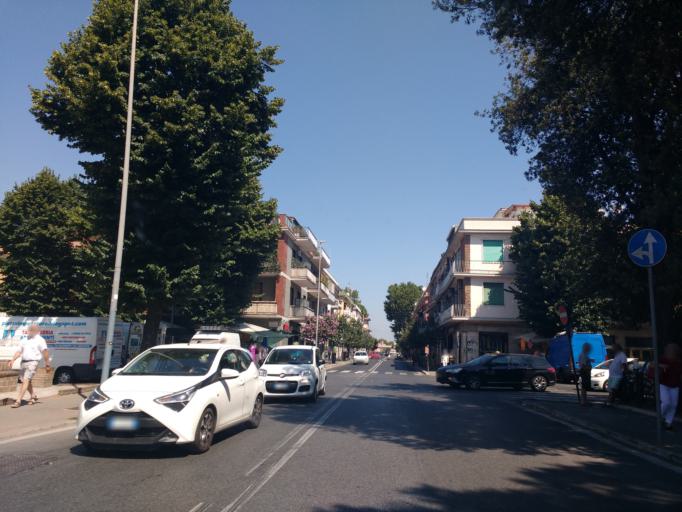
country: IT
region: Latium
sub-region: Citta metropolitana di Roma Capitale
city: Acilia-Castel Fusano-Ostia Antica
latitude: 41.7829
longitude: 12.3654
